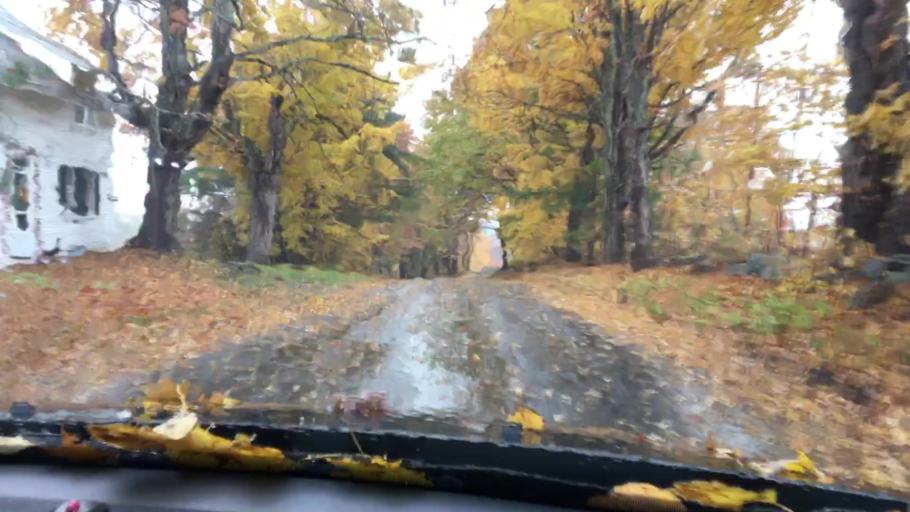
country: US
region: New Hampshire
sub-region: Belknap County
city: Meredith
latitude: 43.6973
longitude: -71.5099
